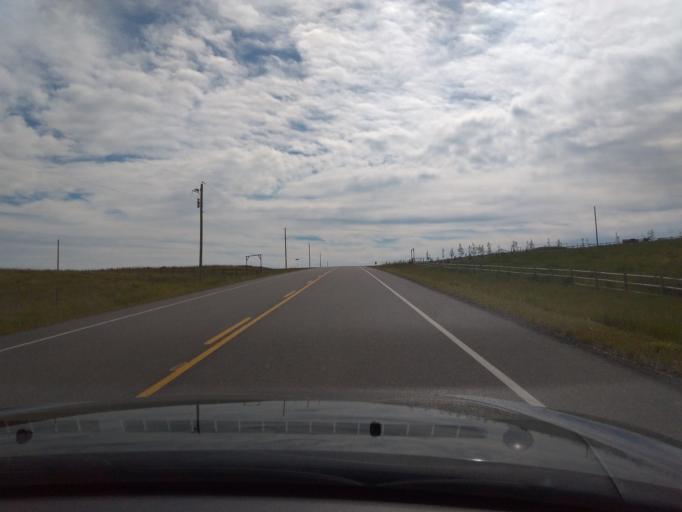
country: CA
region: Alberta
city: Cochrane
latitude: 51.4747
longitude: -114.4137
